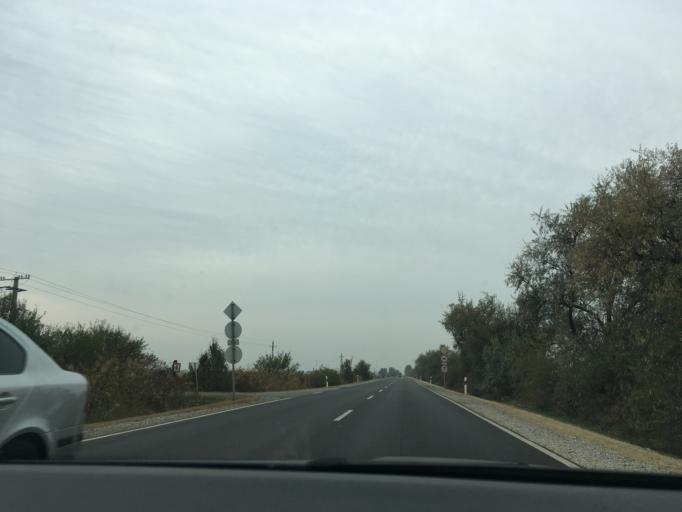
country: HU
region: Jasz-Nagykun-Szolnok
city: Karcag
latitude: 47.3119
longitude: 20.9738
